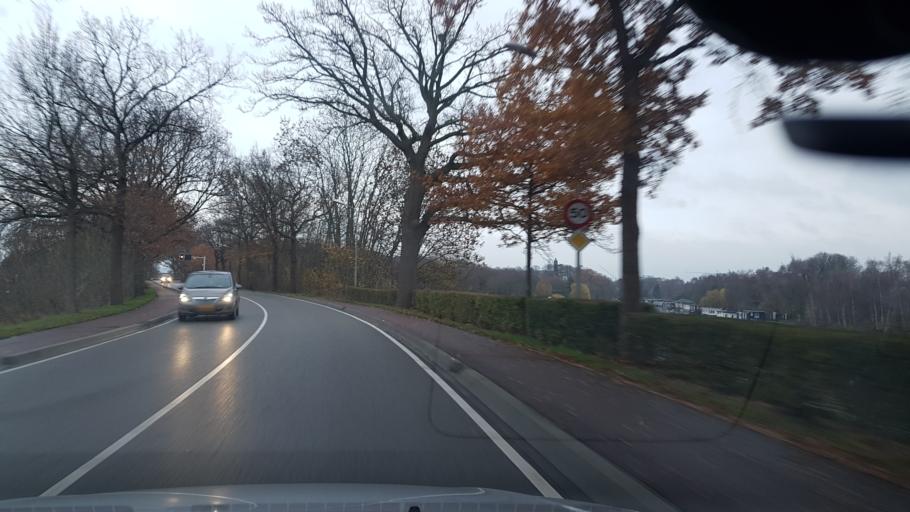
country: NL
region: Limburg
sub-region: Gemeente Maastricht
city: Maastricht
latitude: 50.8703
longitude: 5.6834
